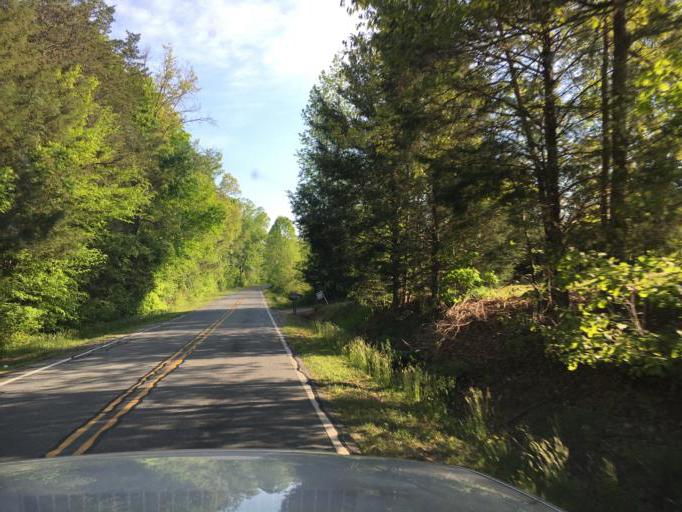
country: US
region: North Carolina
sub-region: Rutherford County
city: Rutherfordton
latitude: 35.3225
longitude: -81.9905
